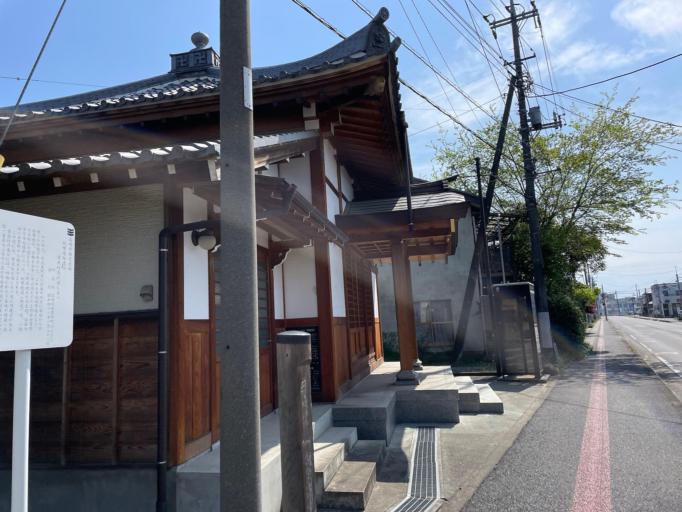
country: JP
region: Gunma
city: Fujioka
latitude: 36.2952
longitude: 139.0547
